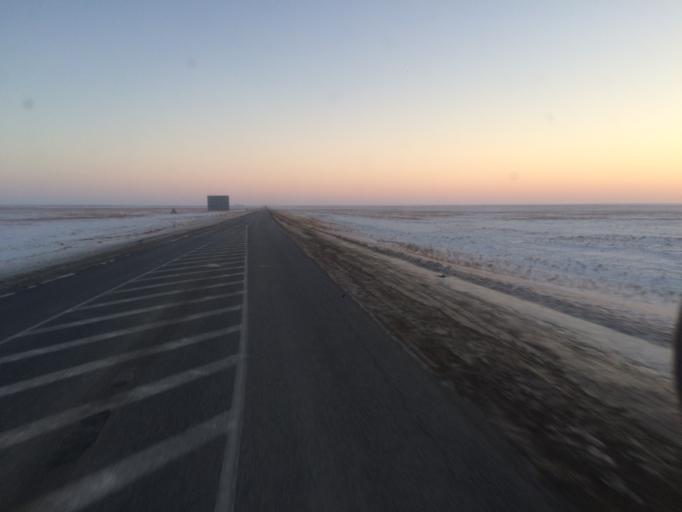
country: KZ
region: Qyzylorda
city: Sekseuil
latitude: 47.4796
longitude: 61.5358
